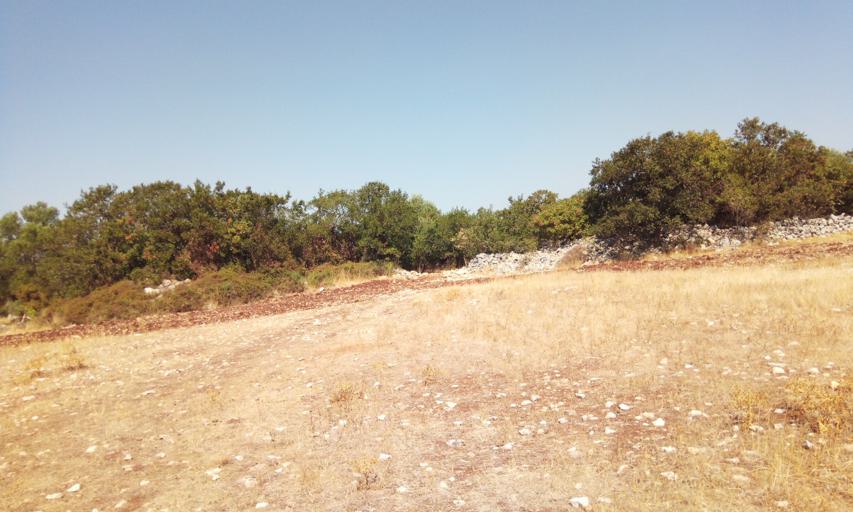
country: IT
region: Apulia
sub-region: Provincia di Bari
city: Gioia del Colle
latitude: 40.8300
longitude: 16.9837
